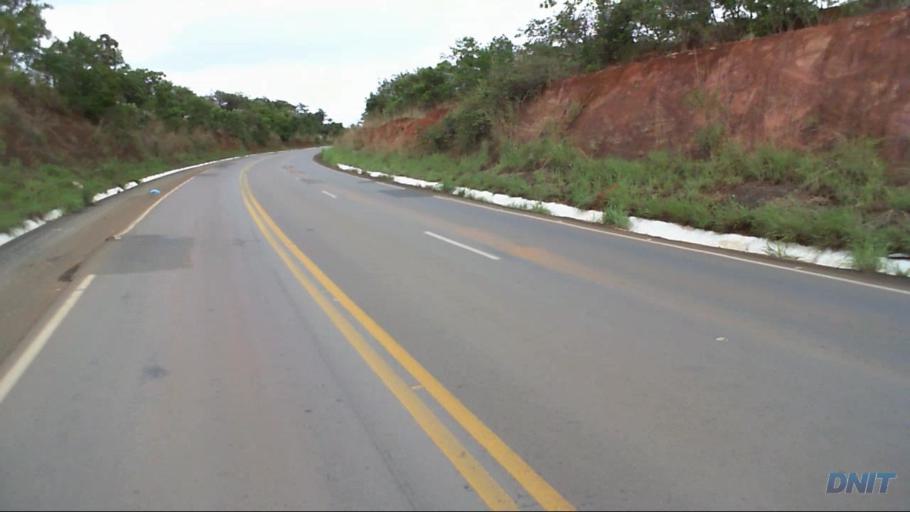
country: BR
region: Goias
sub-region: Barro Alto
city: Barro Alto
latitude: -14.8675
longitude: -49.0134
